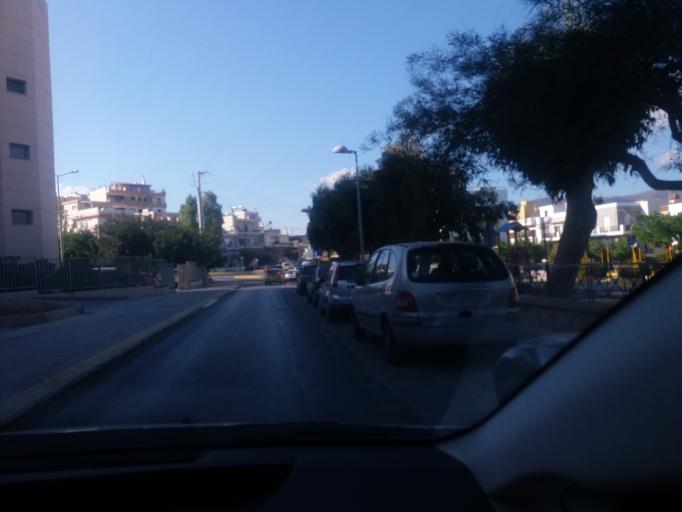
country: GR
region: Crete
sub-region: Nomos Lasithiou
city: Agios Nikolaos
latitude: 35.1945
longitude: 25.7139
